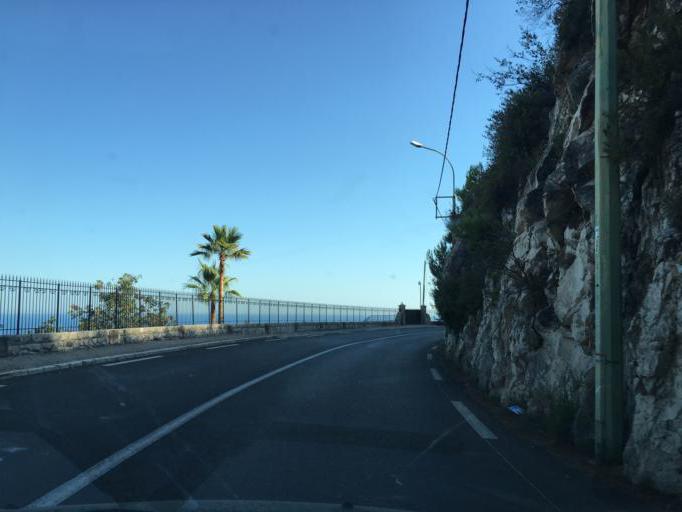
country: FR
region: Provence-Alpes-Cote d'Azur
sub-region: Departement des Alpes-Maritimes
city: Beaulieu-sur-Mer
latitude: 43.7224
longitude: 7.3440
